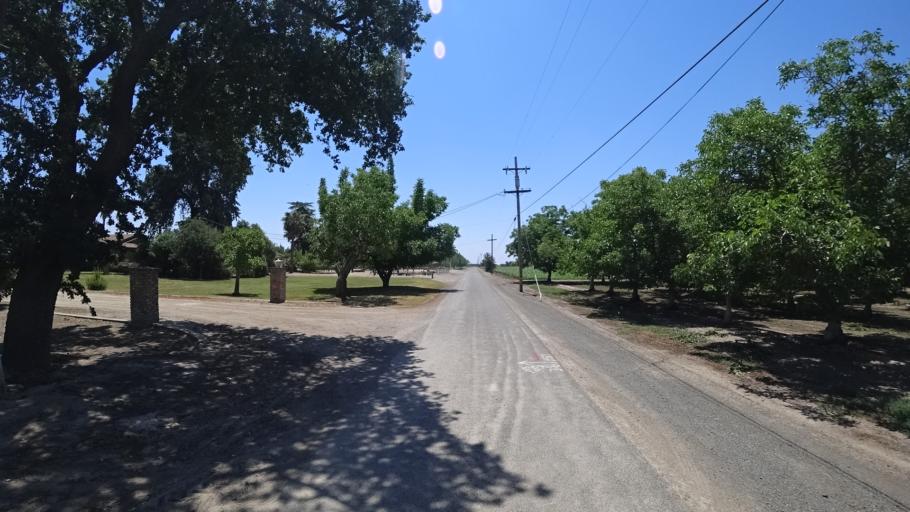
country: US
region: California
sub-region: Fresno County
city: Laton
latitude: 36.3931
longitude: -119.7368
